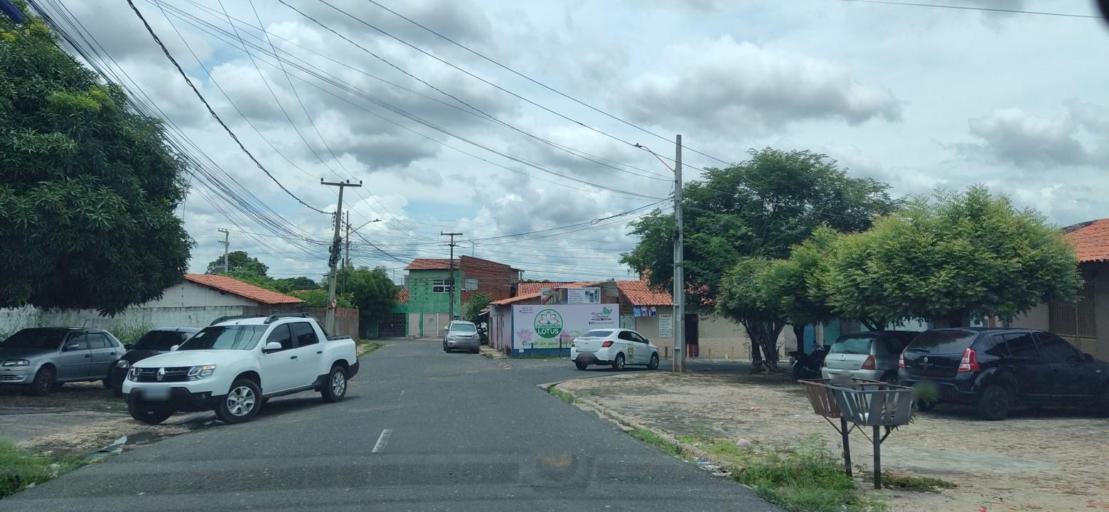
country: BR
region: Piaui
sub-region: Teresina
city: Teresina
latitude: -5.0707
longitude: -42.8060
